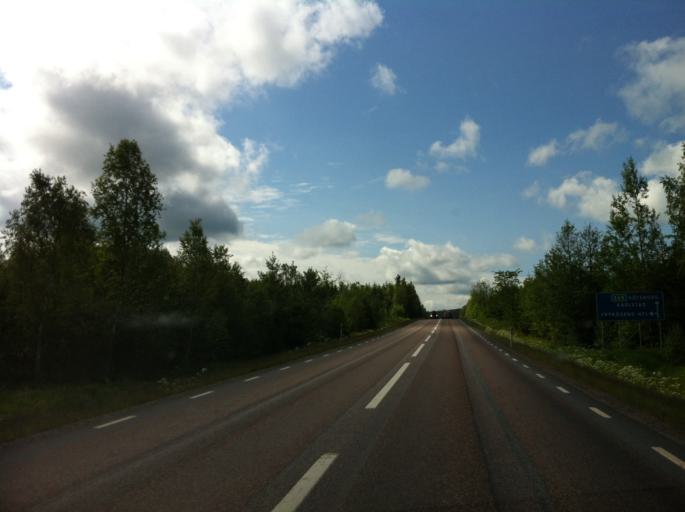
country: SE
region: Vaermland
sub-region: Karlstads Kommun
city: Edsvalla
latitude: 59.6288
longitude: 13.1614
